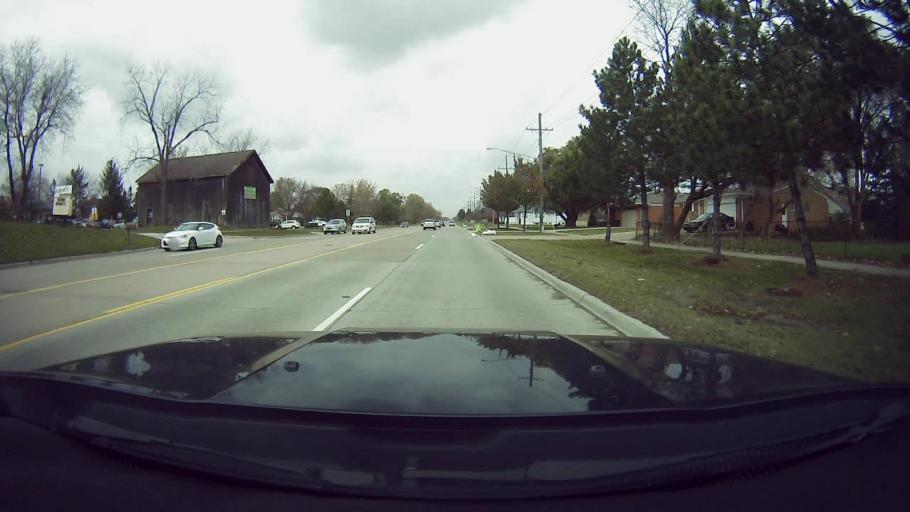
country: US
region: Michigan
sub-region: Macomb County
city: Sterling Heights
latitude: 42.5432
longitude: -83.0689
